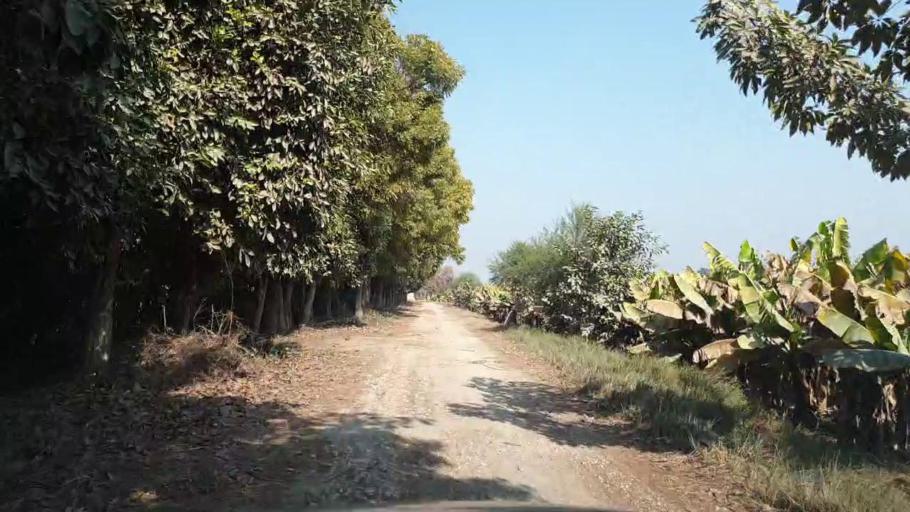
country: PK
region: Sindh
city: Matiari
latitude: 25.5474
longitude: 68.4980
